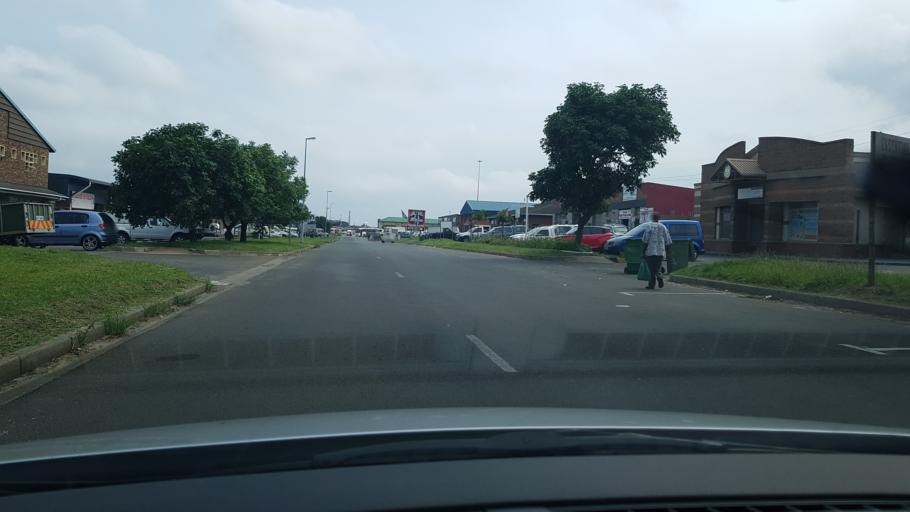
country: ZA
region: KwaZulu-Natal
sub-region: uThungulu District Municipality
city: Richards Bay
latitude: -28.7464
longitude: 32.0479
